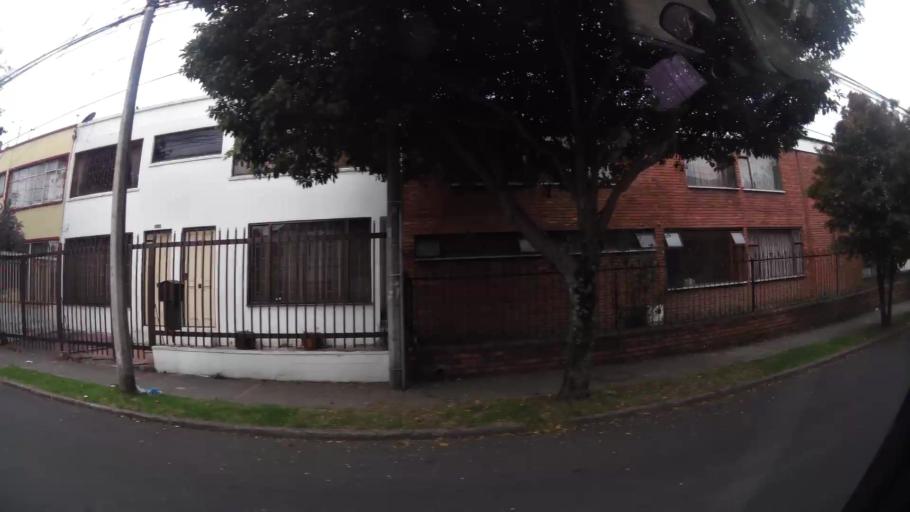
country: CO
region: Bogota D.C.
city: Bogota
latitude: 4.6323
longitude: -74.0768
